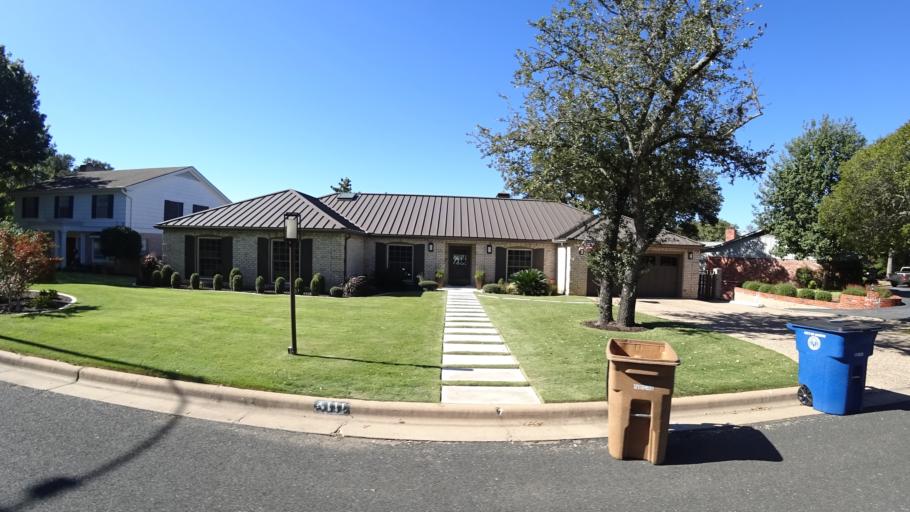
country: US
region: Texas
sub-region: Travis County
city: West Lake Hills
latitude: 30.3590
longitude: -97.7689
